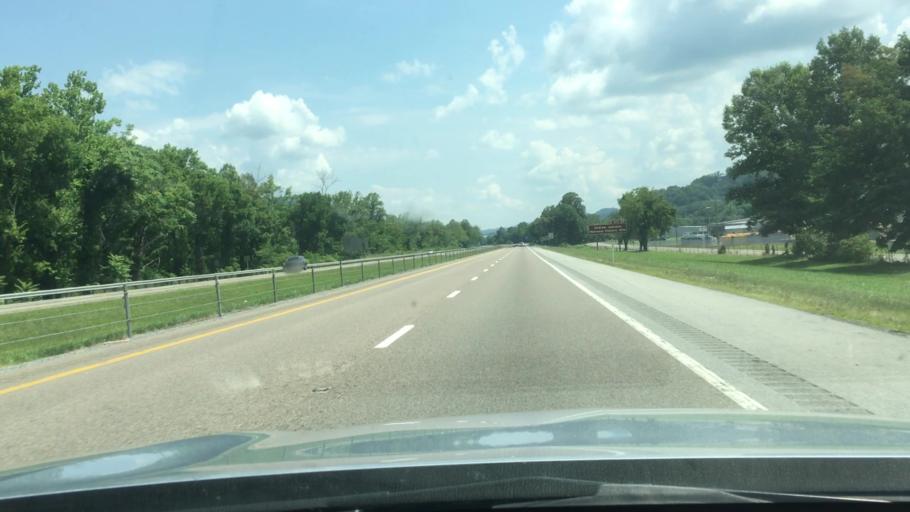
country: US
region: Tennessee
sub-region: Unicoi County
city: Banner Hill
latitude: 36.1299
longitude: -82.4396
